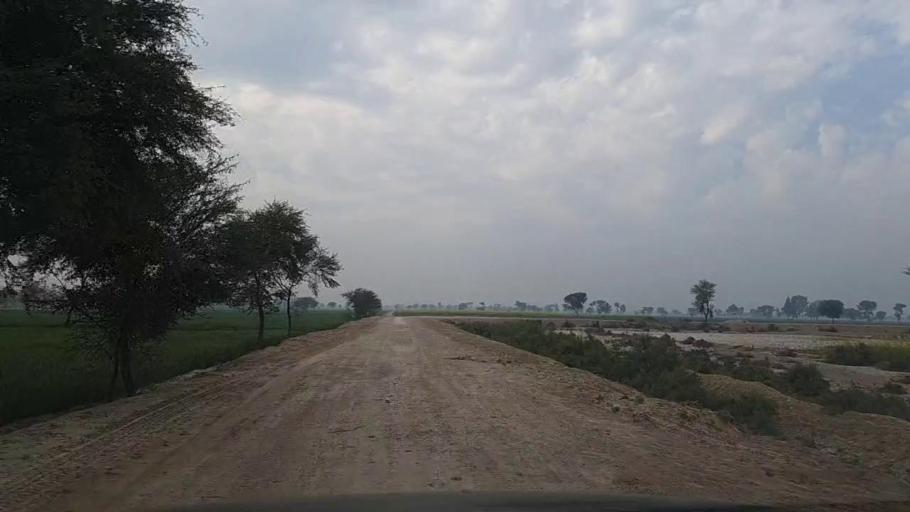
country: PK
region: Sindh
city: Daur
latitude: 26.3654
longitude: 68.3910
